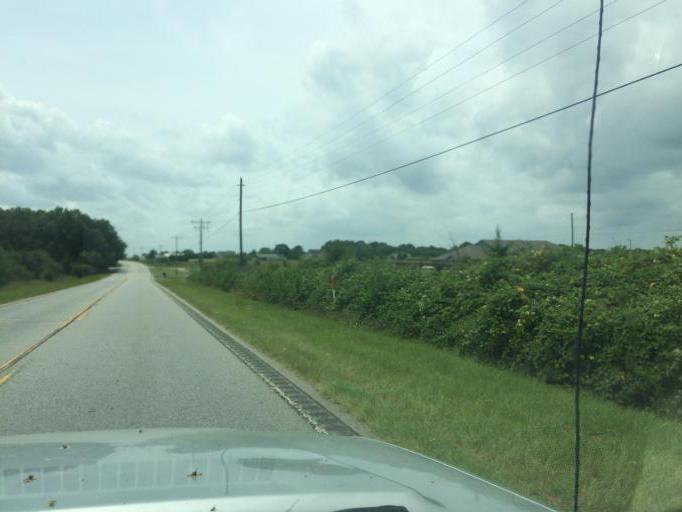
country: US
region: South Carolina
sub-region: Anderson County
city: Centerville
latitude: 34.5054
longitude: -82.7654
